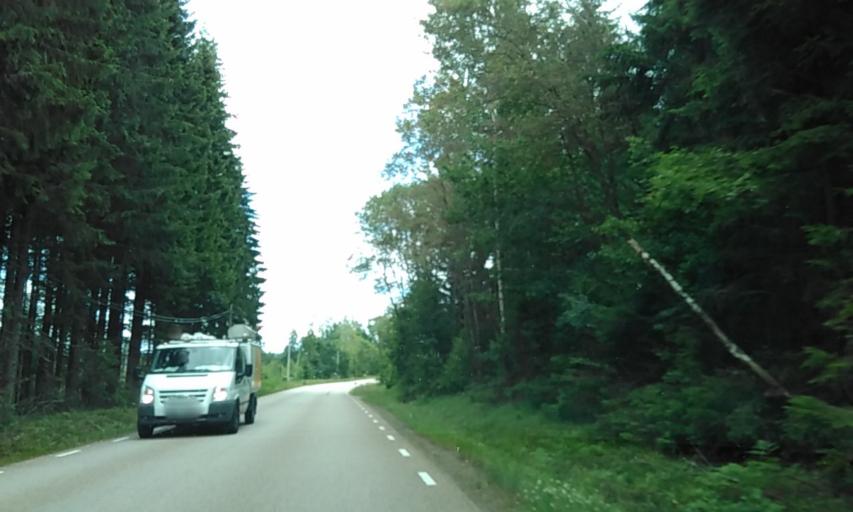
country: SE
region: Vaestra Goetaland
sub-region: Boras Kommun
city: Boras
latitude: 57.8150
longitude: 12.9683
